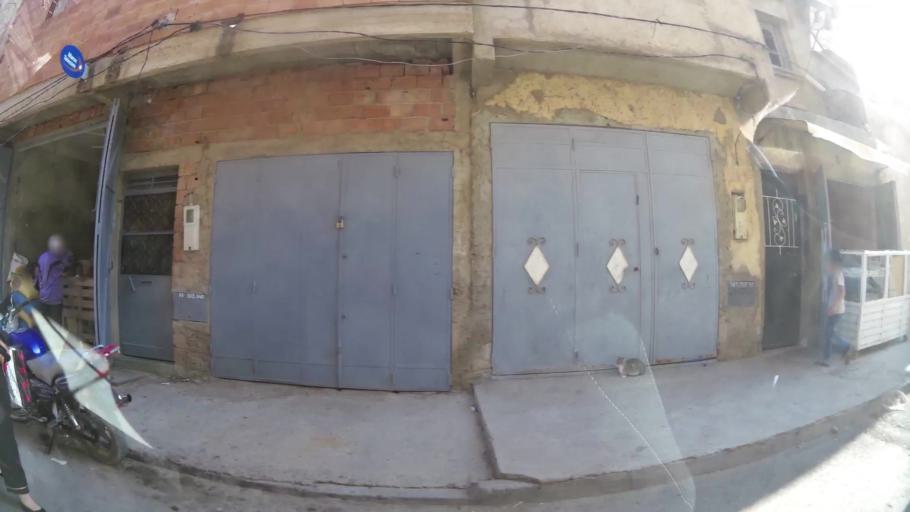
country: MA
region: Oriental
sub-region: Oujda-Angad
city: Oujda
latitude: 34.7145
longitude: -1.8934
